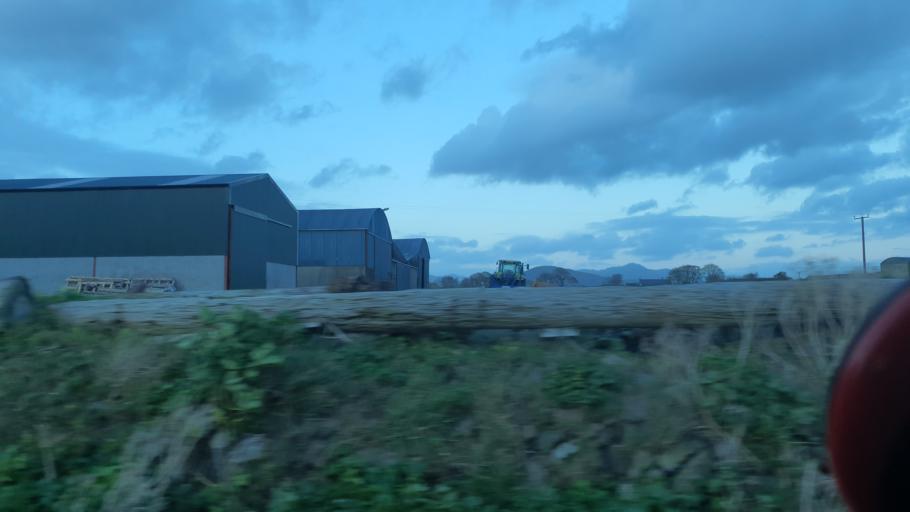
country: IE
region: Leinster
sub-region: Lu
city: Carlingford
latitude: 54.0398
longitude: -6.1017
